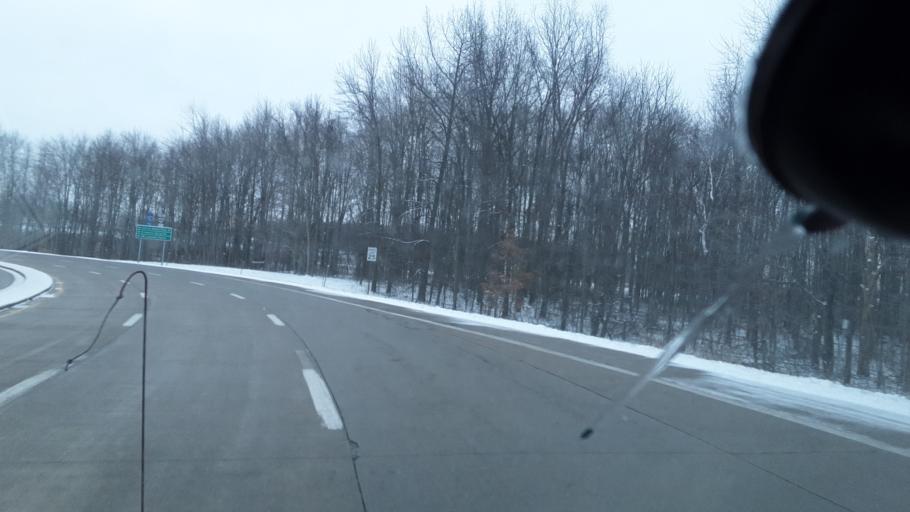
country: US
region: Ohio
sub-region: Trumbull County
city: Lordstown
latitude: 41.1407
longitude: -80.8666
